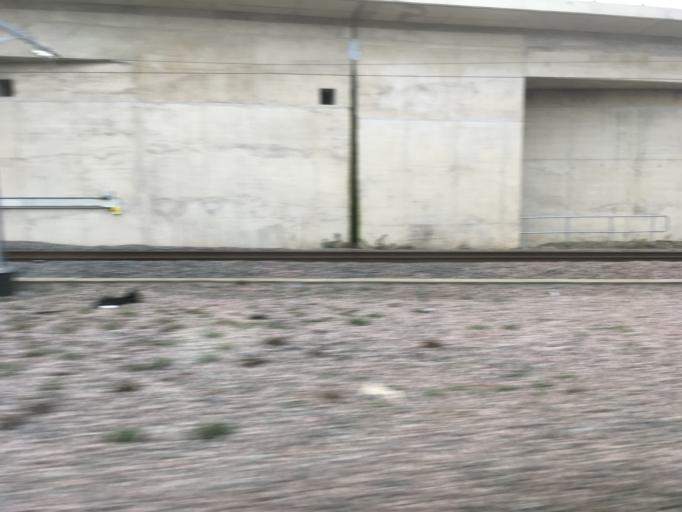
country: GB
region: England
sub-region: Reading
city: Reading
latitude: 51.4616
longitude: -0.9934
